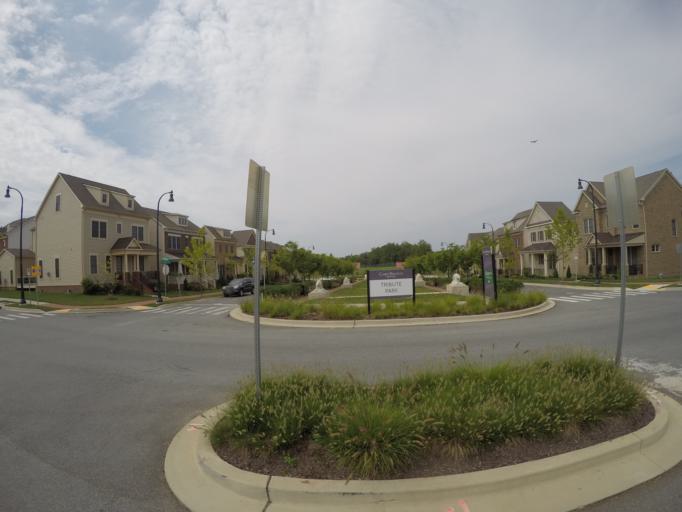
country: US
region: Maryland
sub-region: Montgomery County
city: Clarksburg
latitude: 39.2218
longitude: -77.2876
